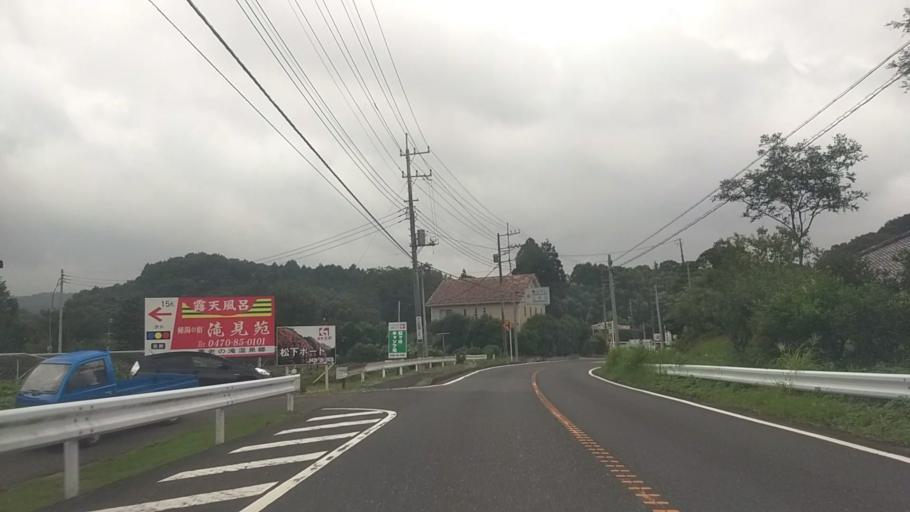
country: JP
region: Chiba
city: Kawaguchi
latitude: 35.2295
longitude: 140.0756
